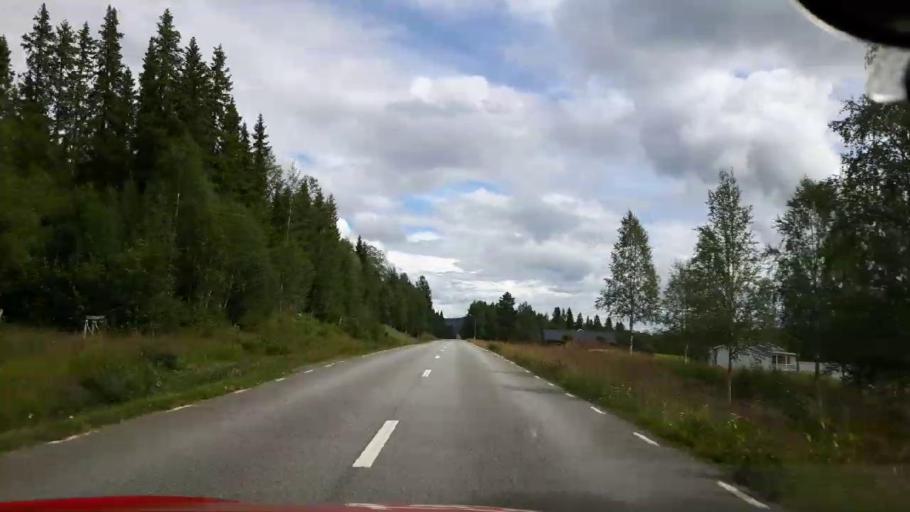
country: NO
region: Nord-Trondelag
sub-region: Lierne
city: Sandvika
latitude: 64.3898
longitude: 14.4157
